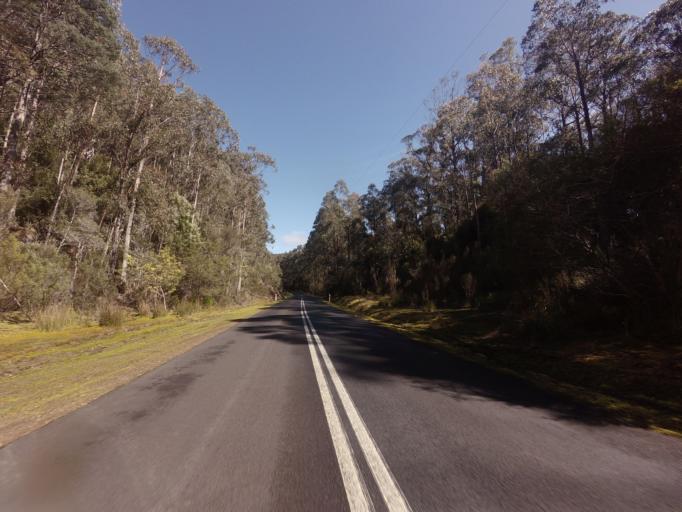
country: AU
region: Tasmania
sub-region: Derwent Valley
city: New Norfolk
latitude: -42.7347
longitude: 146.4832
